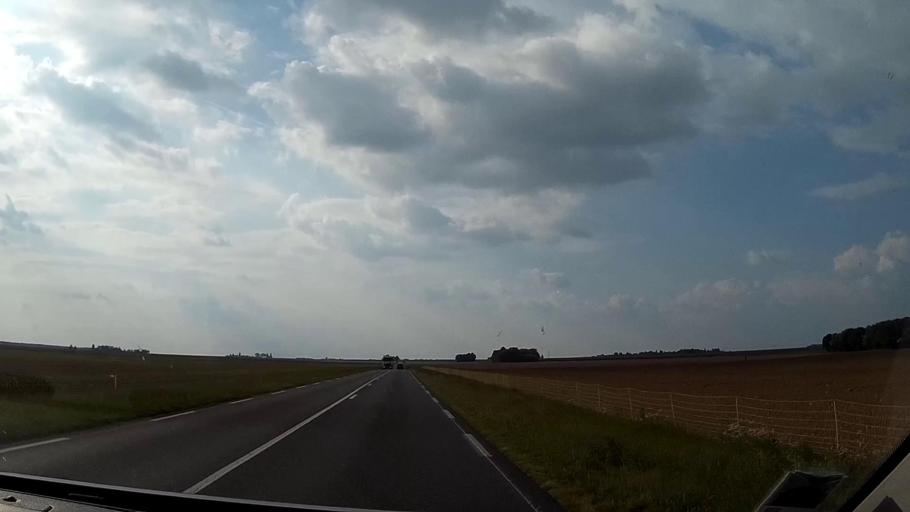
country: FR
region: Centre
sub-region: Departement du Loir-et-Cher
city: Herbault
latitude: 47.6919
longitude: 1.1892
